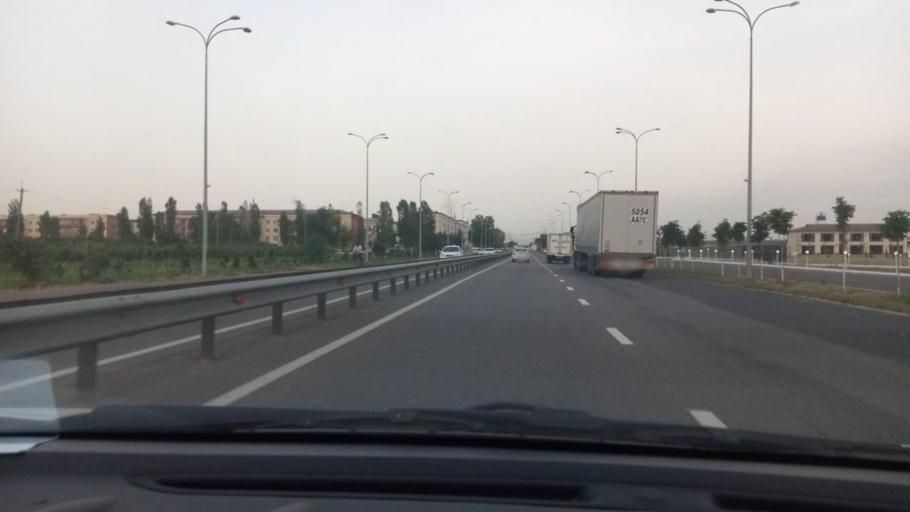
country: UZ
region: Toshkent
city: Ohangaron
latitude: 40.9115
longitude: 69.6176
